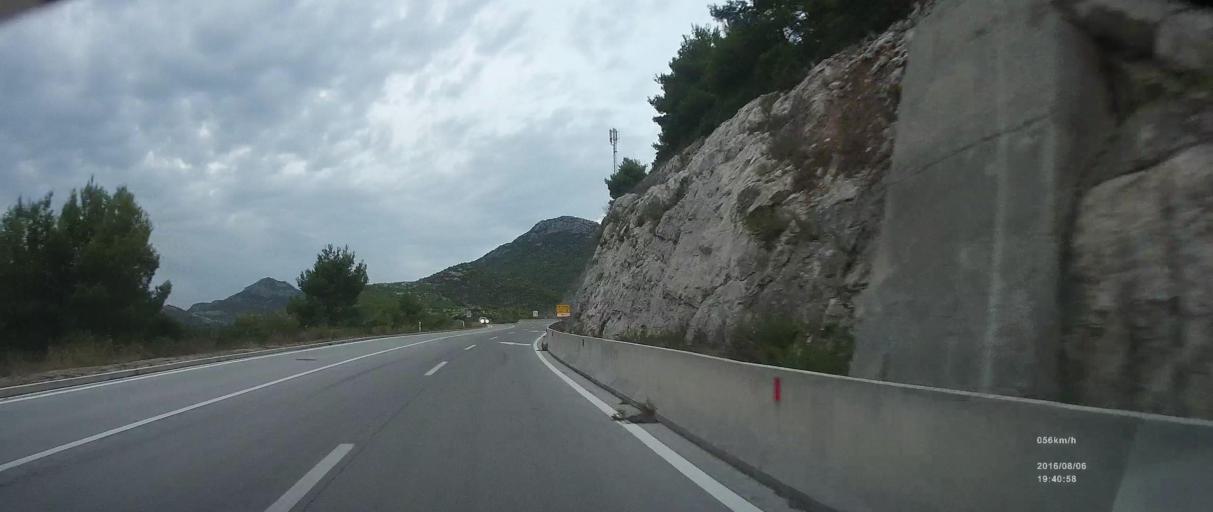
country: HR
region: Dubrovacko-Neretvanska
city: Ston
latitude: 42.8175
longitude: 17.6780
